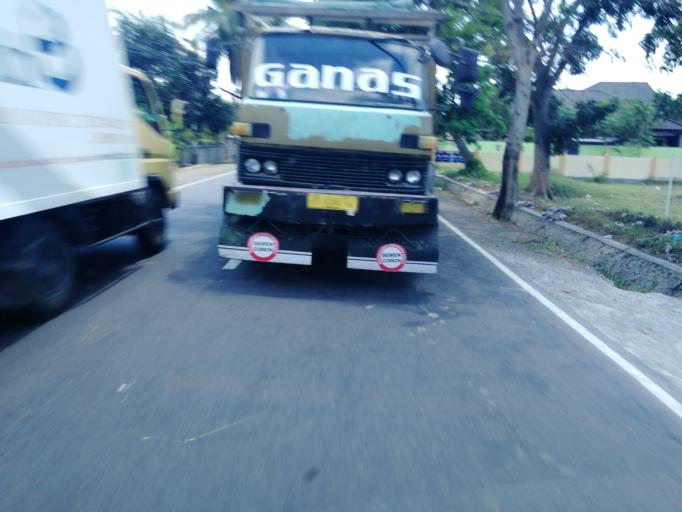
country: ID
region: West Nusa Tenggara
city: Jelateng Timur
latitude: -8.7040
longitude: 116.0910
